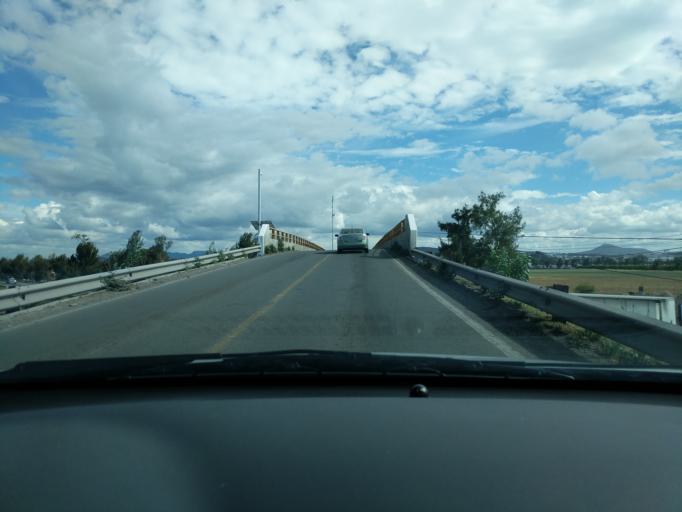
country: MX
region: Queretaro
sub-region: El Marques
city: La Loma
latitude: 20.5928
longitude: -100.2476
